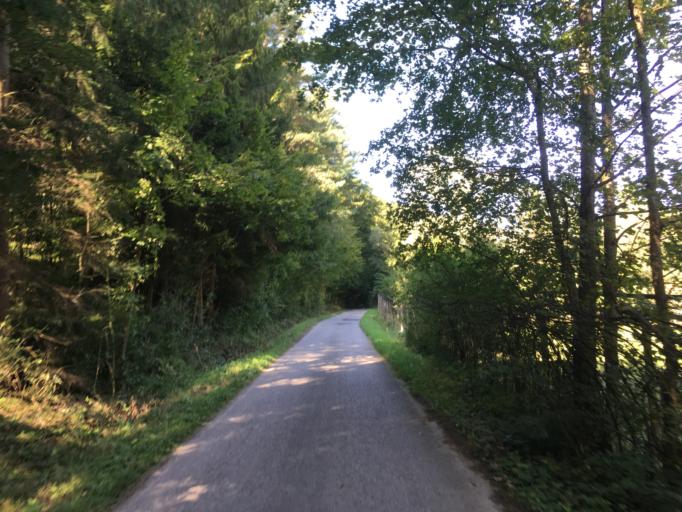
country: SK
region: Trenciansky
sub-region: Okres Povazska Bystrica
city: Povazska Bystrica
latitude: 49.0189
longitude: 18.4396
